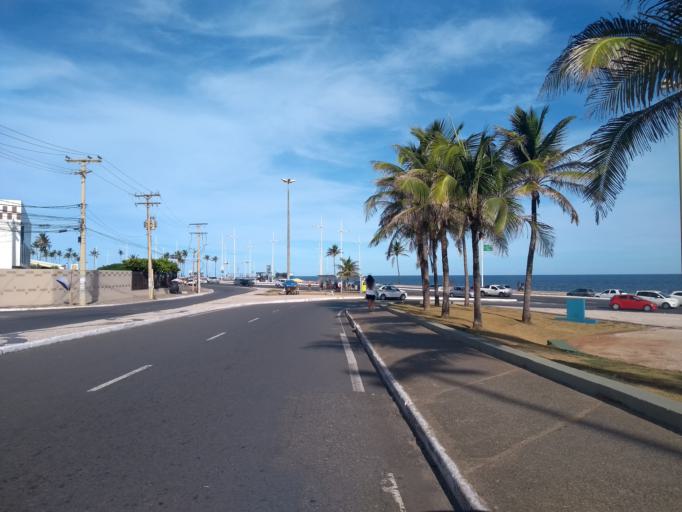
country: BR
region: Bahia
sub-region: Salvador
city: Salvador
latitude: -12.9975
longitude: -38.4456
